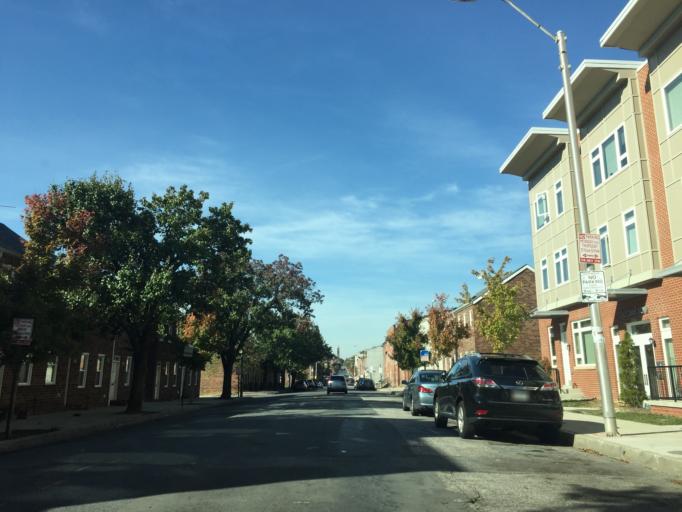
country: US
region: Maryland
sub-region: City of Baltimore
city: Baltimore
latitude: 39.2900
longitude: -76.6314
